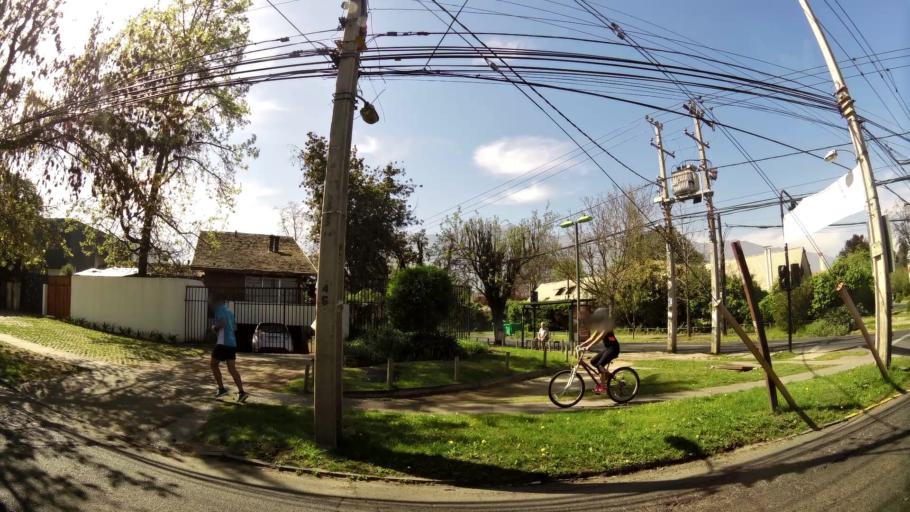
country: CL
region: Santiago Metropolitan
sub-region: Provincia de Santiago
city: Villa Presidente Frei, Nunoa, Santiago, Chile
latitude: -33.4422
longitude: -70.5533
